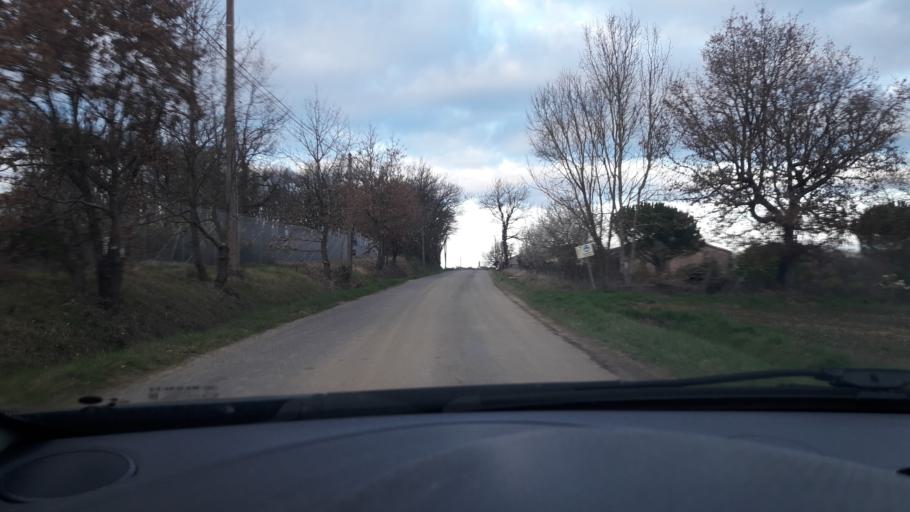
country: FR
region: Midi-Pyrenees
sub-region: Departement de la Haute-Garonne
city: Launac
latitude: 43.7265
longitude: 1.1056
